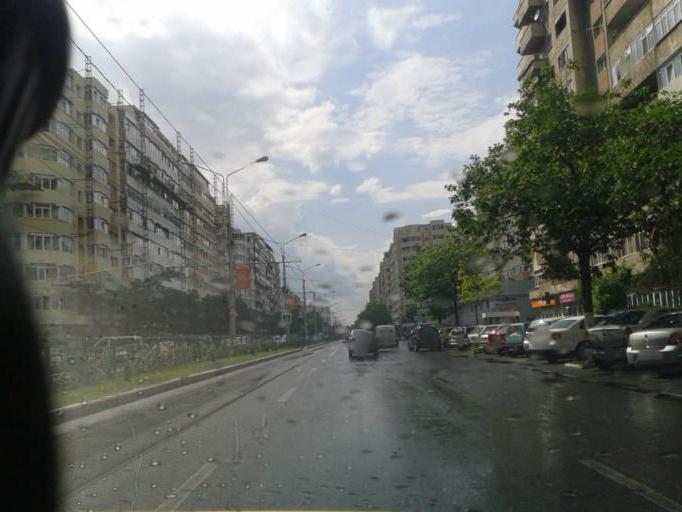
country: RO
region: Prahova
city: Ploiesti
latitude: 44.9487
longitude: 26.0076
